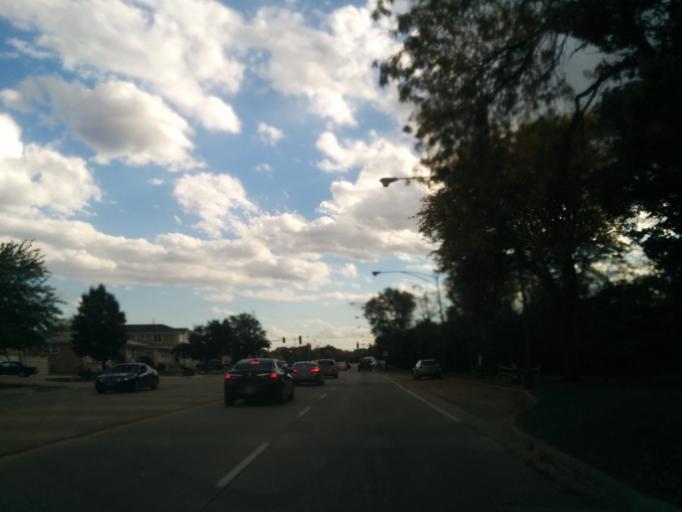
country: US
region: Illinois
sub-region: Cook County
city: Norridge
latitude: 41.9678
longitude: -87.8466
